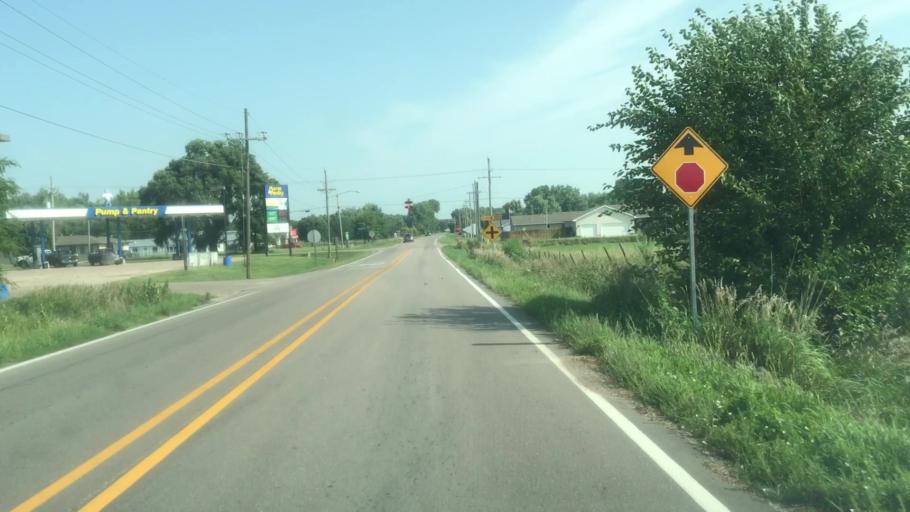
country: US
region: Nebraska
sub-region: Hall County
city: Grand Island
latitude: 40.9148
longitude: -98.3018
